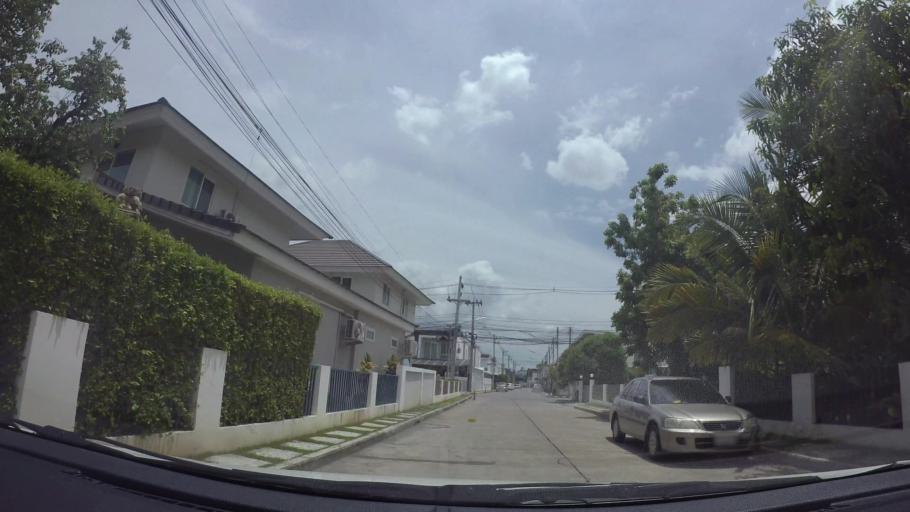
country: TH
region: Chiang Mai
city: Chiang Mai
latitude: 18.7682
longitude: 98.9927
